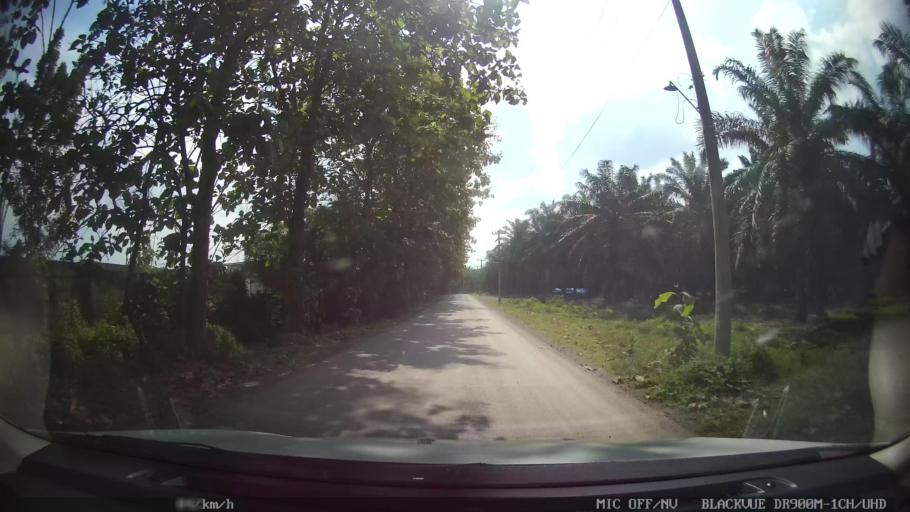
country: ID
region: North Sumatra
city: Binjai
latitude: 3.6351
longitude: 98.5319
